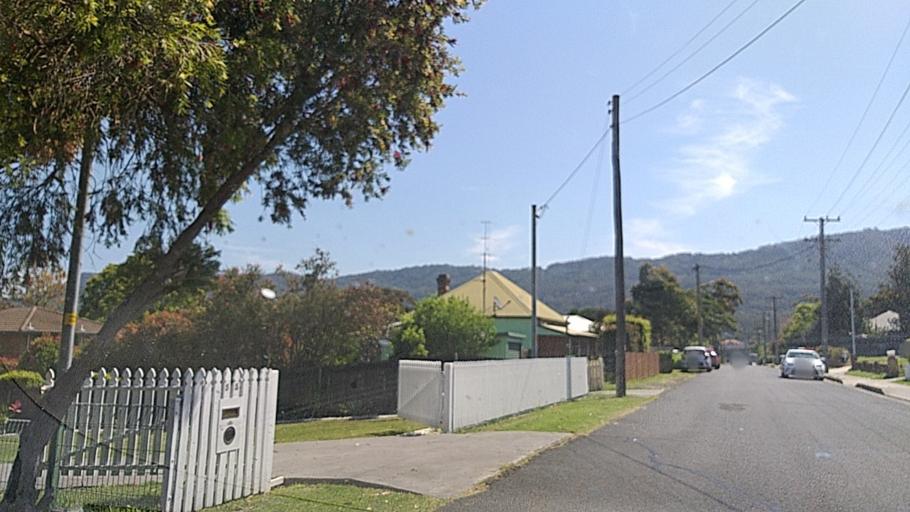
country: AU
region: New South Wales
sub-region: Wollongong
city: Bulli
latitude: -34.3391
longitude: 150.9164
